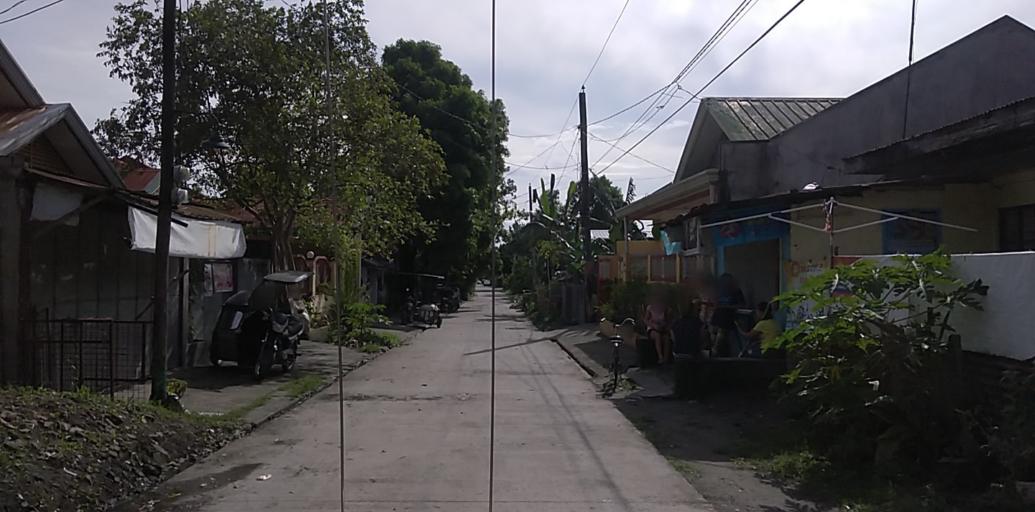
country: PH
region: Central Luzon
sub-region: Province of Pampanga
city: Angeles City
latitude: 15.1308
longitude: 120.5621
